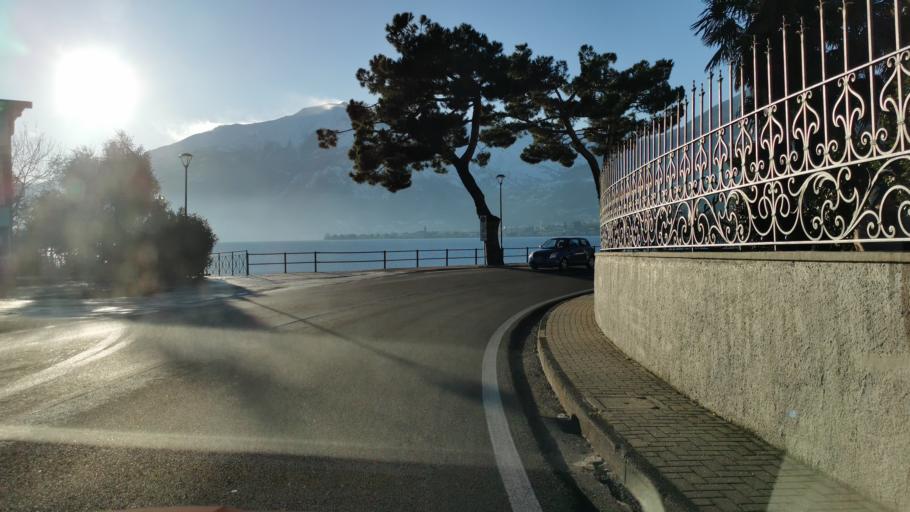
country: IT
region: Lombardy
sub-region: Provincia di Como
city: Domaso
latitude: 46.1498
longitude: 9.3293
